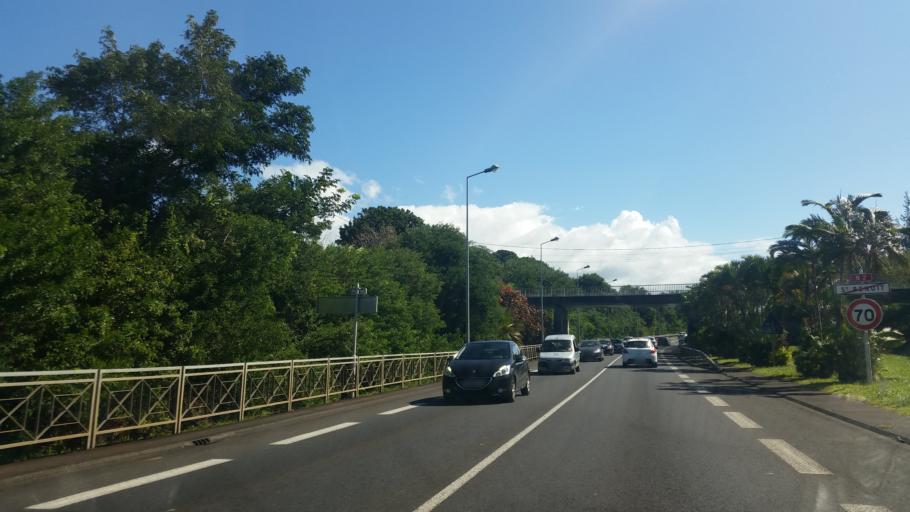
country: RE
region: Reunion
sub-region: Reunion
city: Saint-Benoit
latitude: -21.0402
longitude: 55.7110
